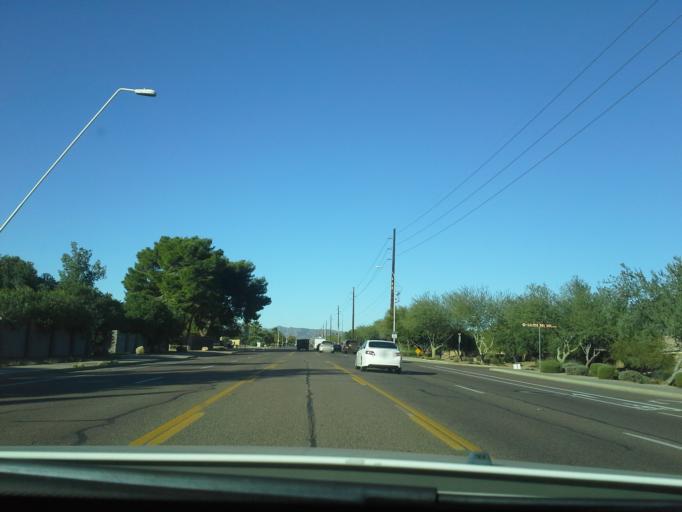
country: US
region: Arizona
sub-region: Maricopa County
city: San Carlos
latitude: 33.3495
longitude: -111.8783
